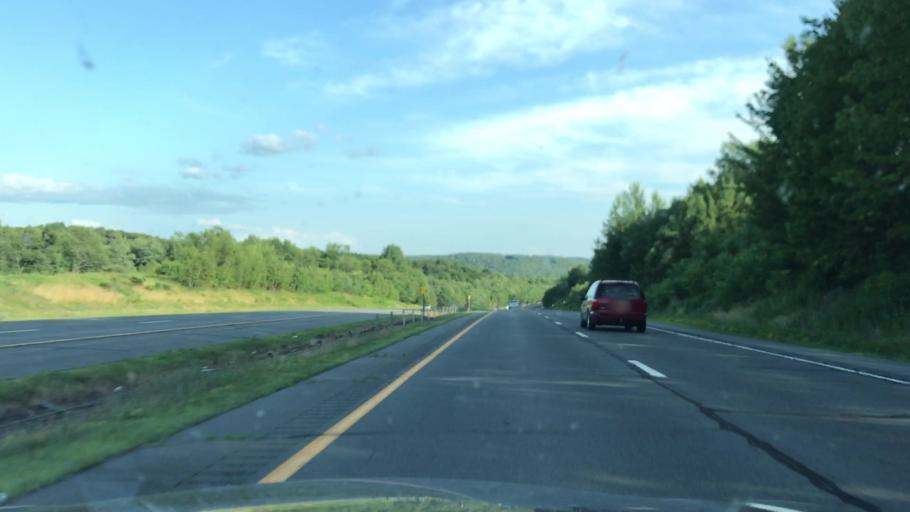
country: US
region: New York
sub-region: Sullivan County
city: Liberty
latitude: 41.7378
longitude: -74.7307
